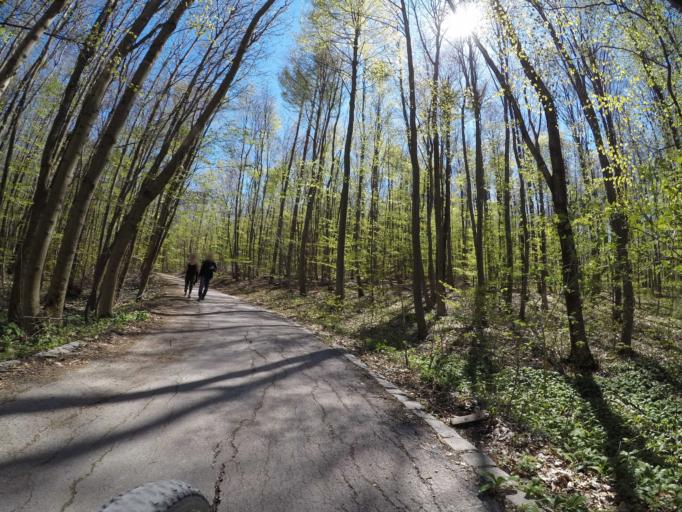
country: AT
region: Lower Austria
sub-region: Politischer Bezirk Modling
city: Hinterbruehl
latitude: 48.0542
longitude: 16.2463
